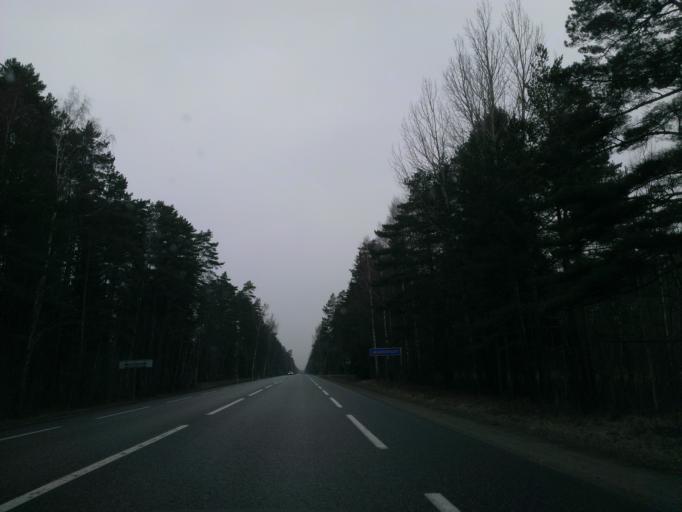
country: LV
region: Saulkrastu
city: Saulkrasti
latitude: 57.4748
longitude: 24.4341
